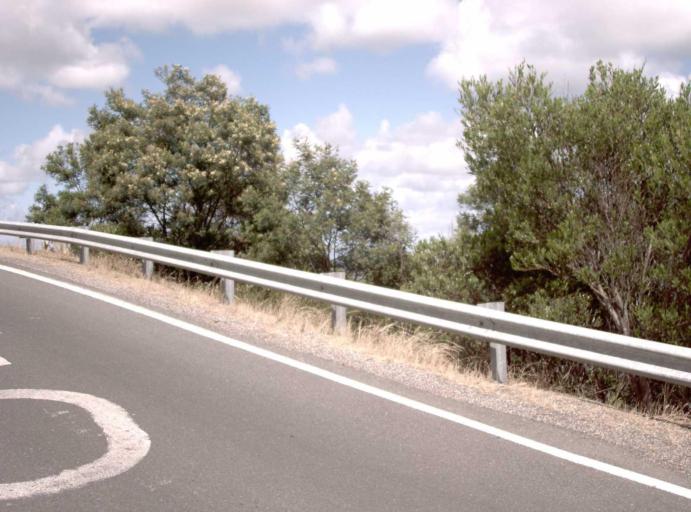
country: AU
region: Victoria
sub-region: Mornington Peninsula
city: McCrae
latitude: -38.3503
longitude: 144.9477
